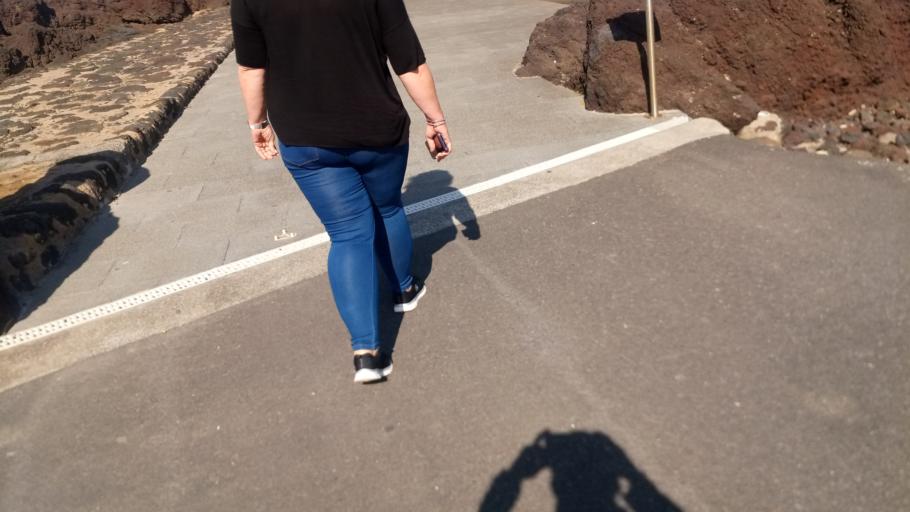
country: PT
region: Azores
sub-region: Praia da Vitoria
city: Biscoitos
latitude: 38.8025
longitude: -27.2573
